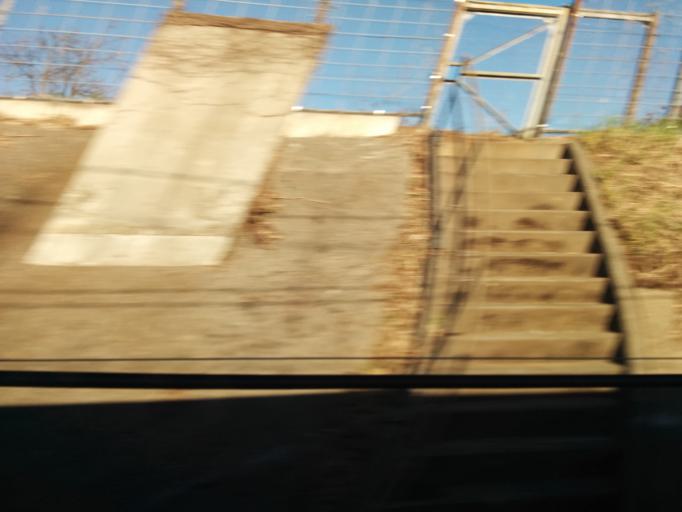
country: JP
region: Kanagawa
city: Minami-rinkan
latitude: 35.4274
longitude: 139.4543
